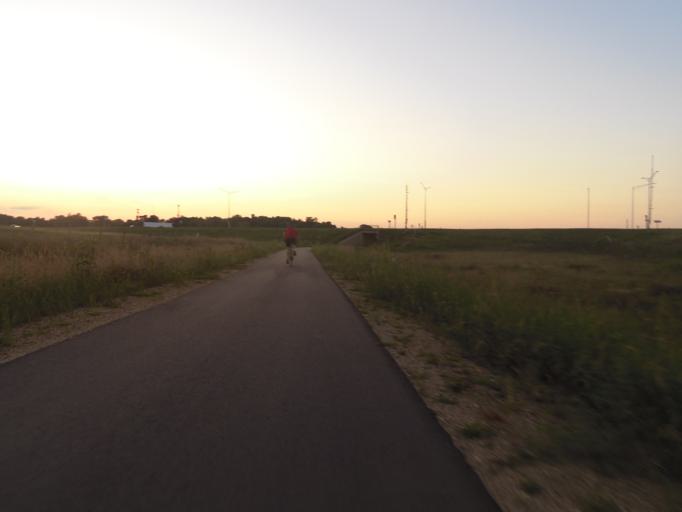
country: US
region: Minnesota
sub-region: Washington County
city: Stillwater
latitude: 45.0584
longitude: -92.7821
